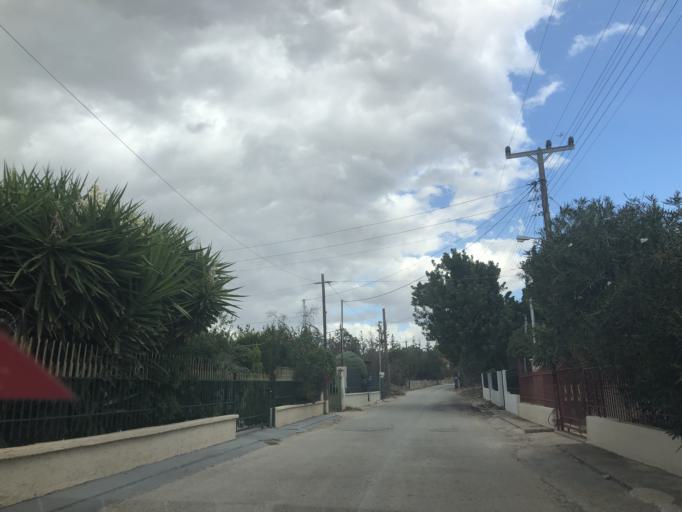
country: GR
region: Attica
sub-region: Nomarchia Anatolikis Attikis
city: Agia Marina
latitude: 37.8218
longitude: 23.8446
